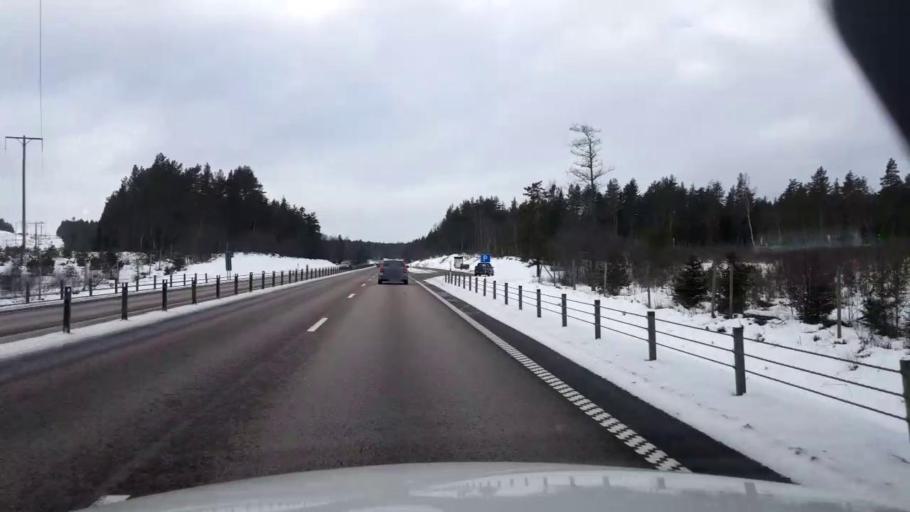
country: SE
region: Gaevleborg
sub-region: Hudiksvalls Kommun
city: Hudiksvall
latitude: 61.7922
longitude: 17.1547
